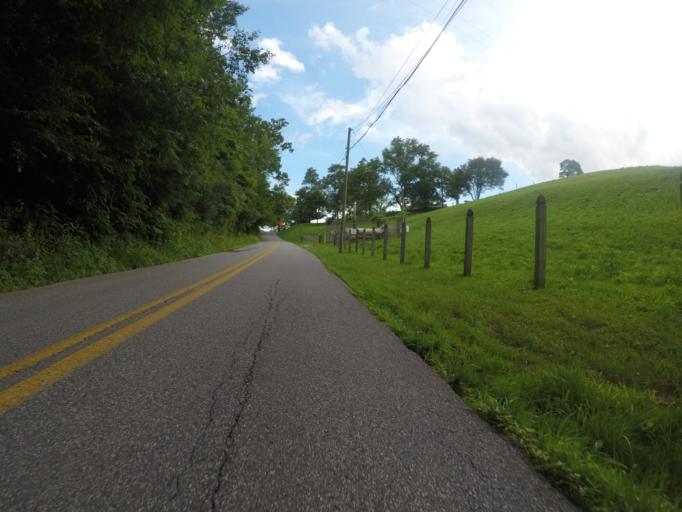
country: US
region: West Virginia
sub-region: Cabell County
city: Pea Ridge
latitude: 38.3895
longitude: -82.3612
